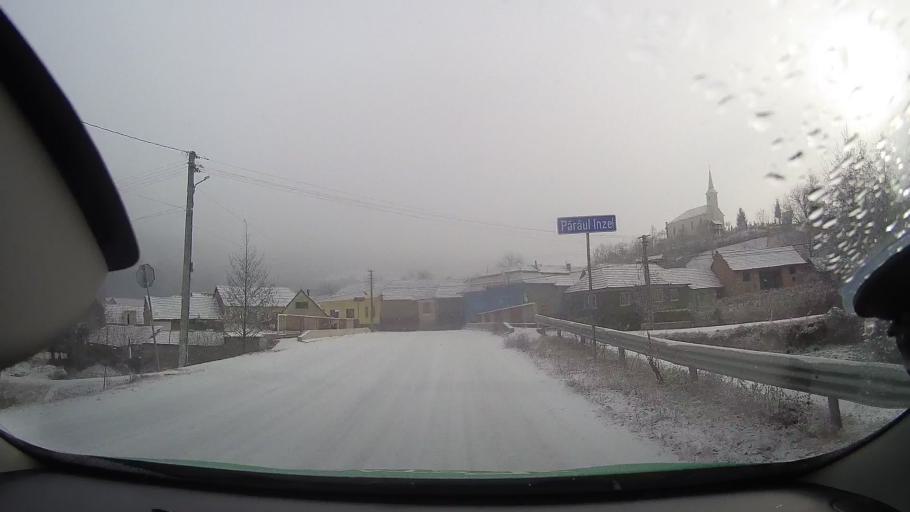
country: RO
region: Alba
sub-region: Comuna Livezile
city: Livezile
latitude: 46.3659
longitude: 23.6023
